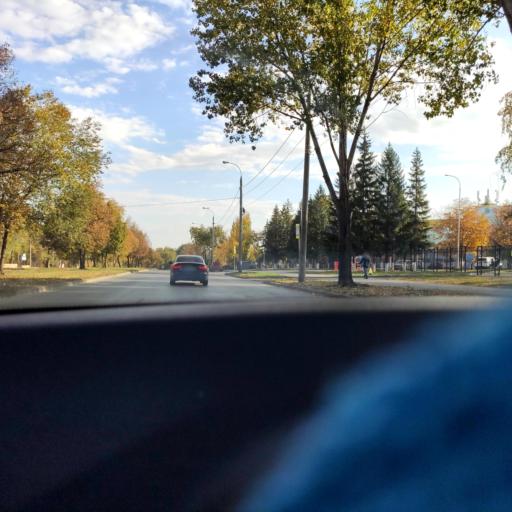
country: RU
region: Samara
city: Samara
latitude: 53.2226
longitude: 50.2358
